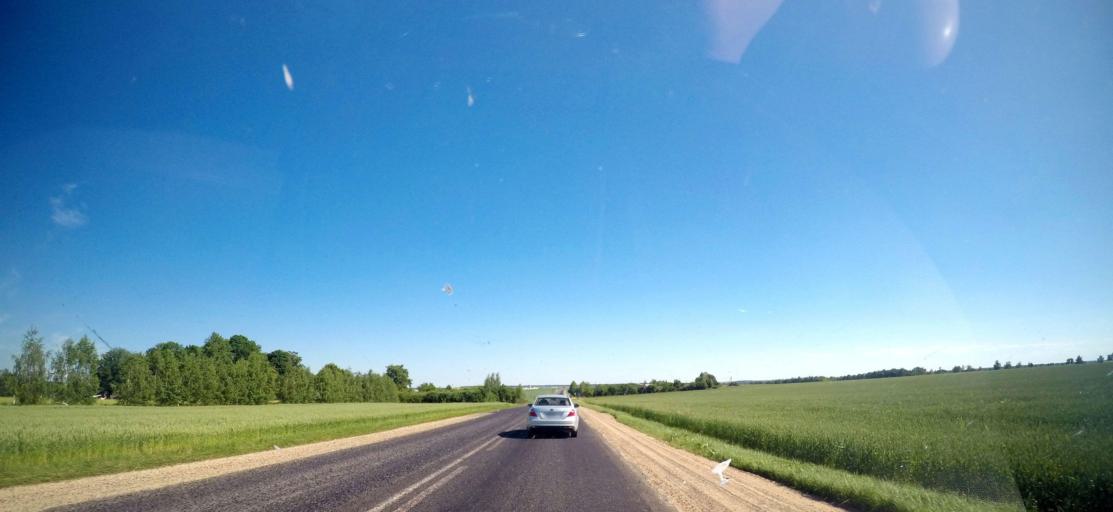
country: BY
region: Grodnenskaya
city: Vyalikaya Byerastavitsa
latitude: 53.2139
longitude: 24.0017
